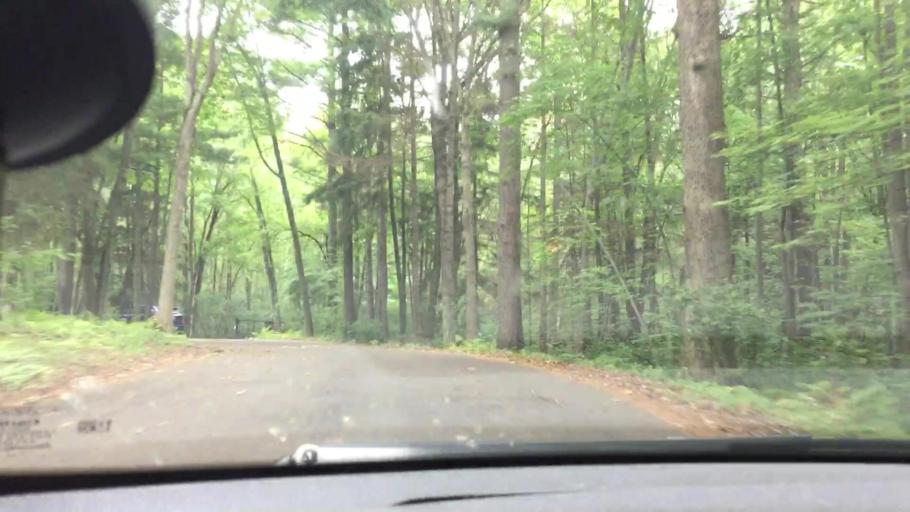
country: US
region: Wisconsin
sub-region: Chippewa County
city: Chippewa Falls
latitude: 44.9563
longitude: -91.4015
